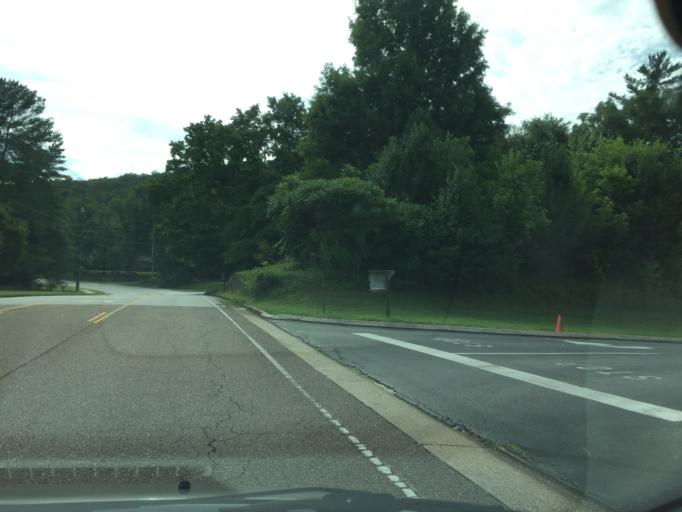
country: US
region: Tennessee
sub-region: Hamilton County
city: Collegedale
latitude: 35.0435
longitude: -85.0467
